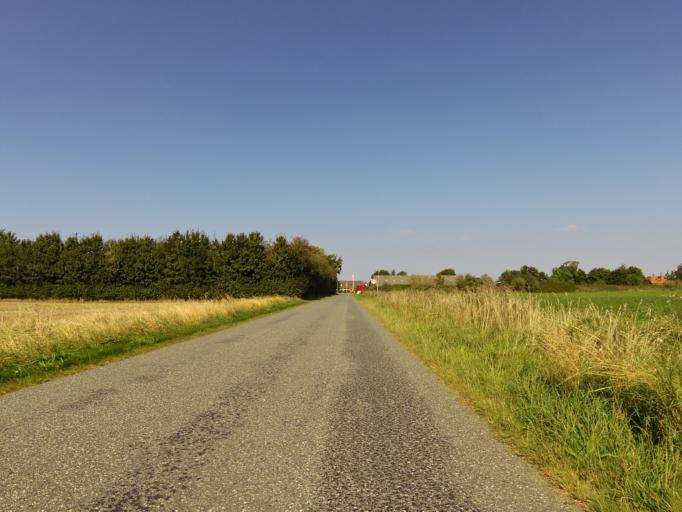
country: DK
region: South Denmark
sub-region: Vejen Kommune
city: Rodding
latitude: 55.3438
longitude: 9.1297
